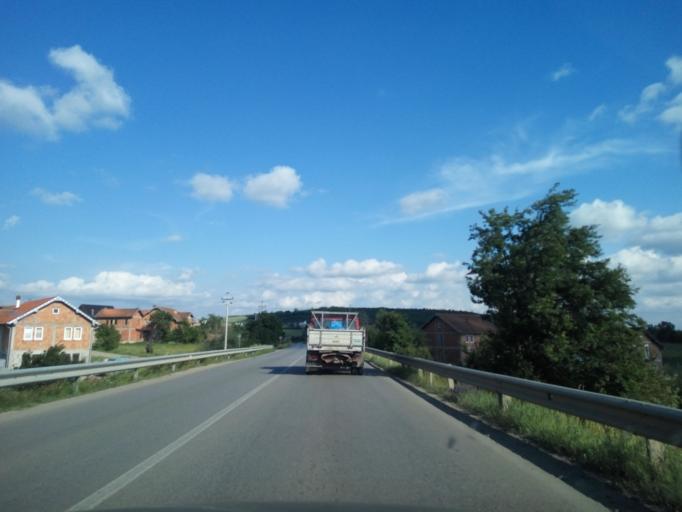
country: XK
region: Pec
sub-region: Komuna e Klines
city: Klina
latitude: 42.5912
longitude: 20.6642
